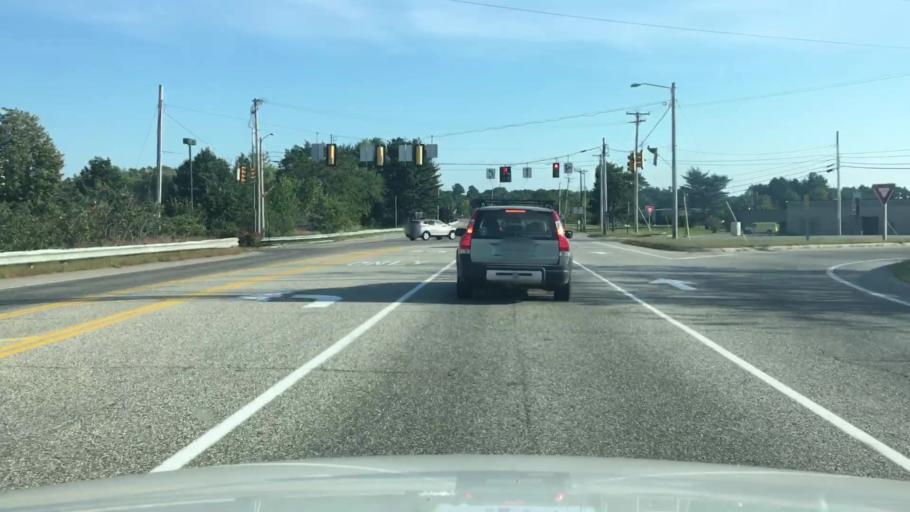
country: US
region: Maine
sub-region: Cumberland County
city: Falmouth
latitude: 43.7332
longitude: -70.2965
